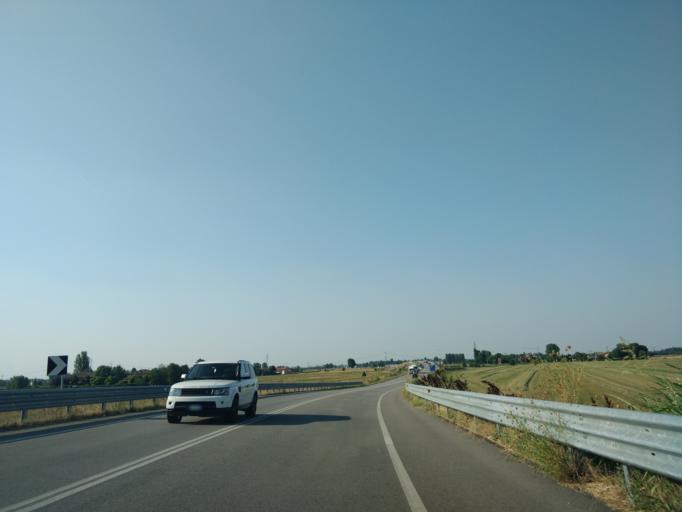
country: IT
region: Emilia-Romagna
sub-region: Provincia di Bologna
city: Castel Maggiore
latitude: 44.5829
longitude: 11.3461
